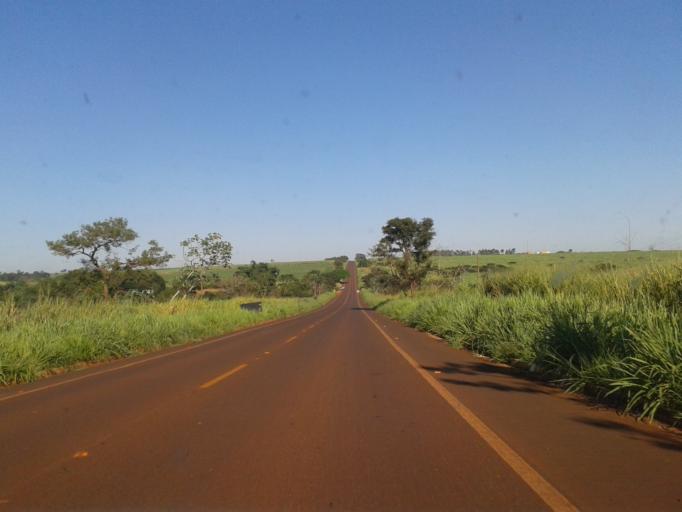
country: BR
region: Minas Gerais
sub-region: Capinopolis
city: Capinopolis
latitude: -18.7021
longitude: -49.6657
